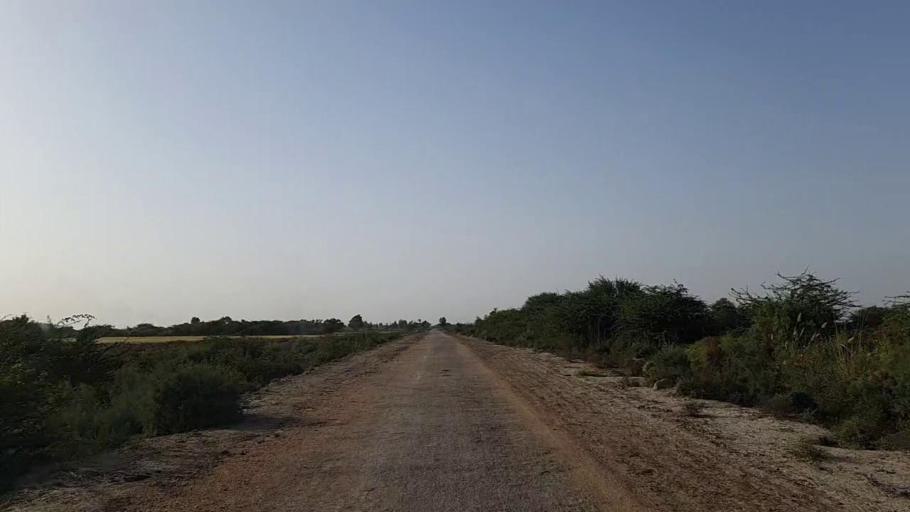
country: PK
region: Sindh
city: Jati
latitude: 24.3229
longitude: 68.1663
